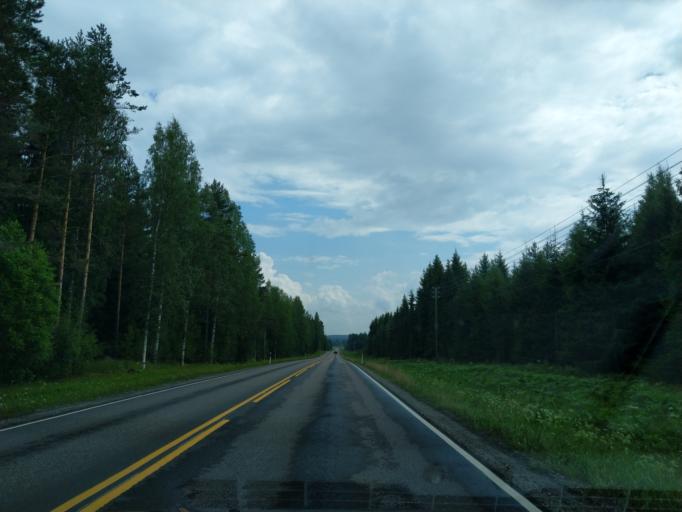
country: FI
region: South Karelia
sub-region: Imatra
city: Parikkala
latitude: 61.6156
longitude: 29.4480
